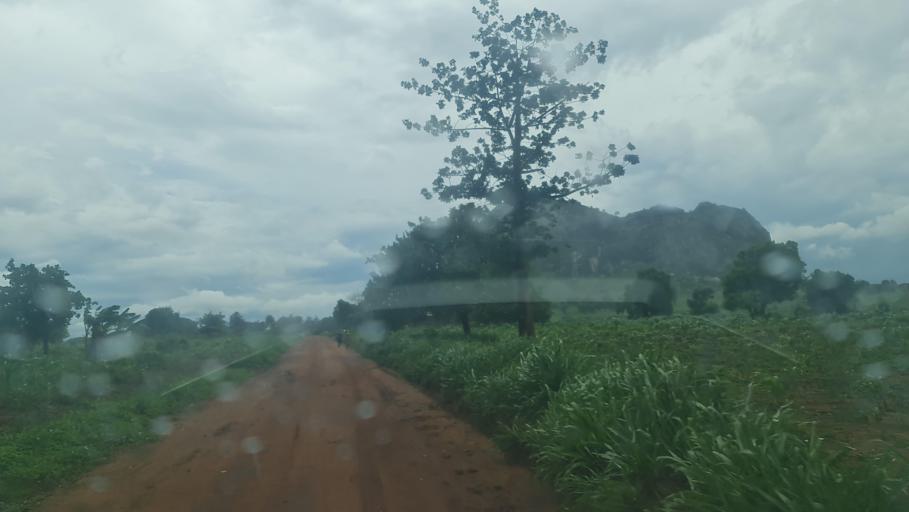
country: MW
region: Southern Region
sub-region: Nsanje District
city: Nsanje
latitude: -17.3989
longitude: 35.5876
